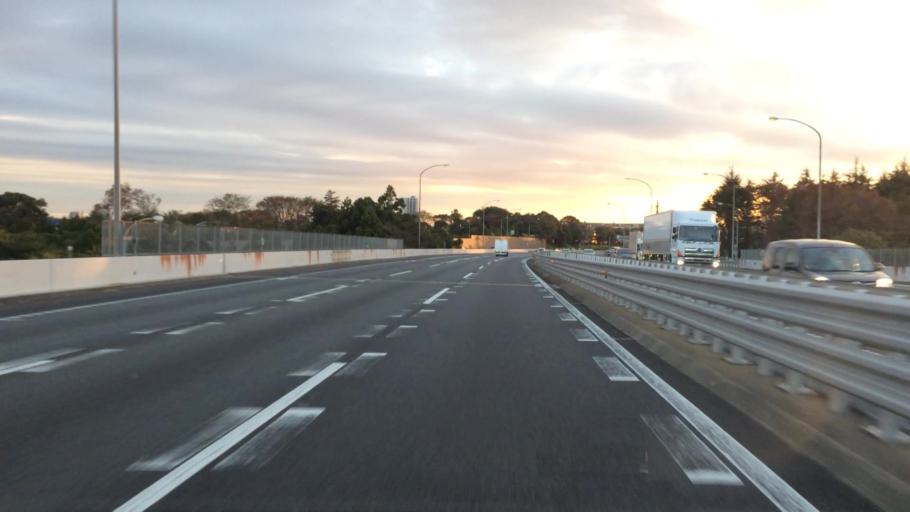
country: JP
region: Chiba
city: Chiba
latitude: 35.6607
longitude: 140.1007
